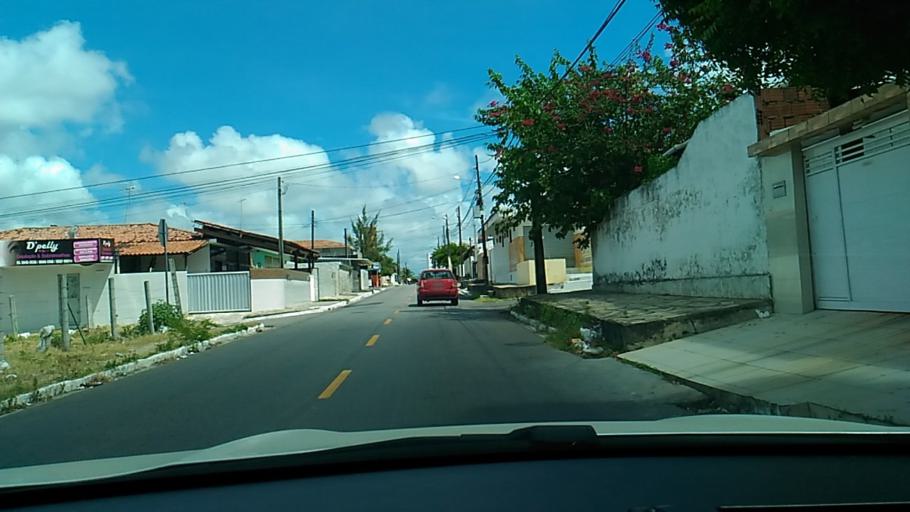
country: BR
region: Paraiba
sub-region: Joao Pessoa
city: Joao Pessoa
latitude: -7.1580
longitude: -34.8415
